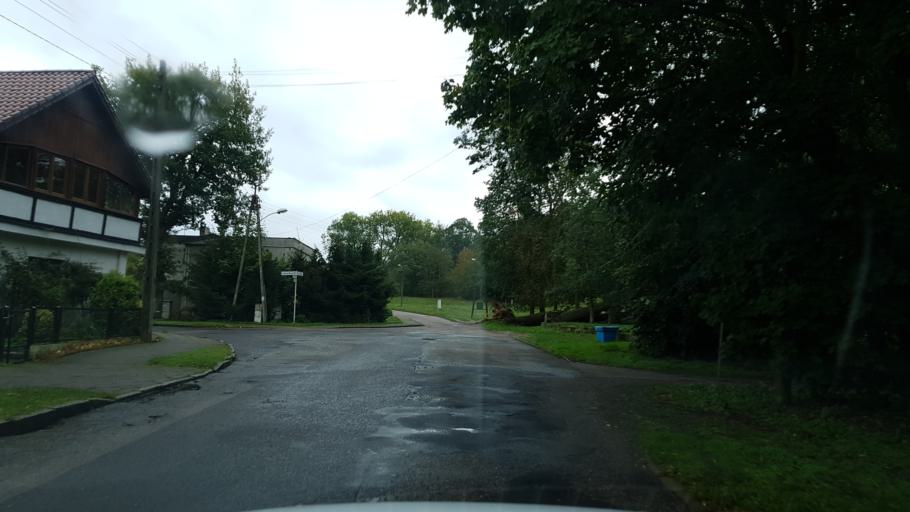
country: PL
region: West Pomeranian Voivodeship
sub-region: Powiat kamienski
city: Wolin
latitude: 53.8337
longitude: 14.6102
